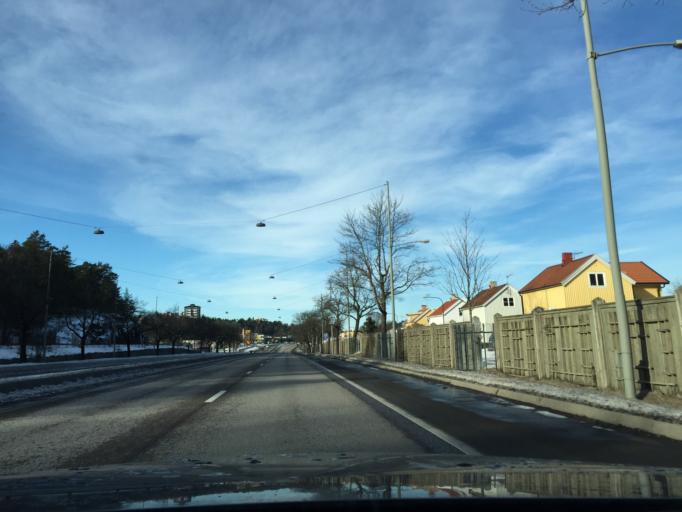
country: SE
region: Stockholm
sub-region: Stockholms Kommun
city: Bromma
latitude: 59.3445
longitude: 17.9009
